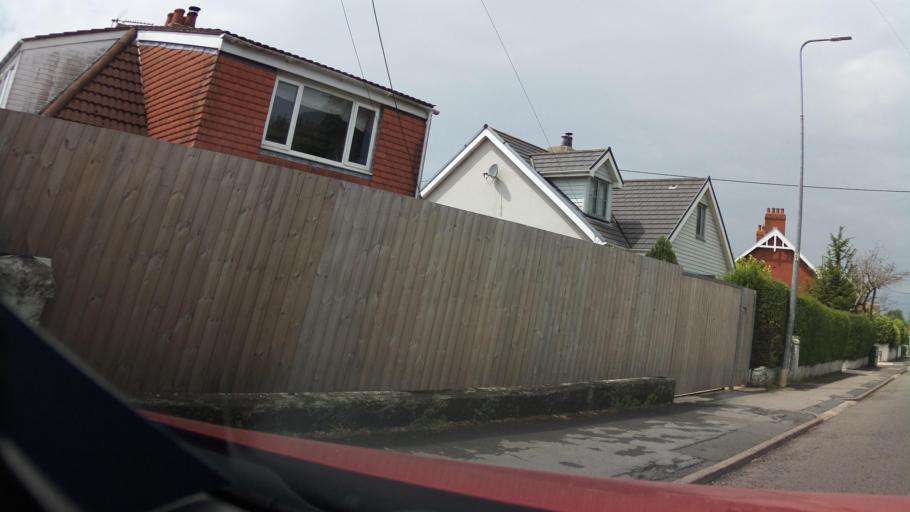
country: GB
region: Wales
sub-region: Vale of Glamorgan
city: Dinas Powys
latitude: 51.4048
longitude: -3.2116
